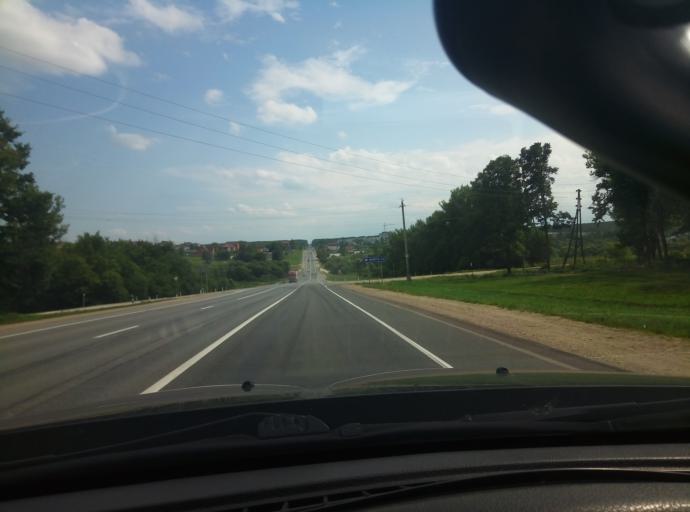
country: RU
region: Tula
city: Gorelki
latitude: 54.3073
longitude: 37.5697
